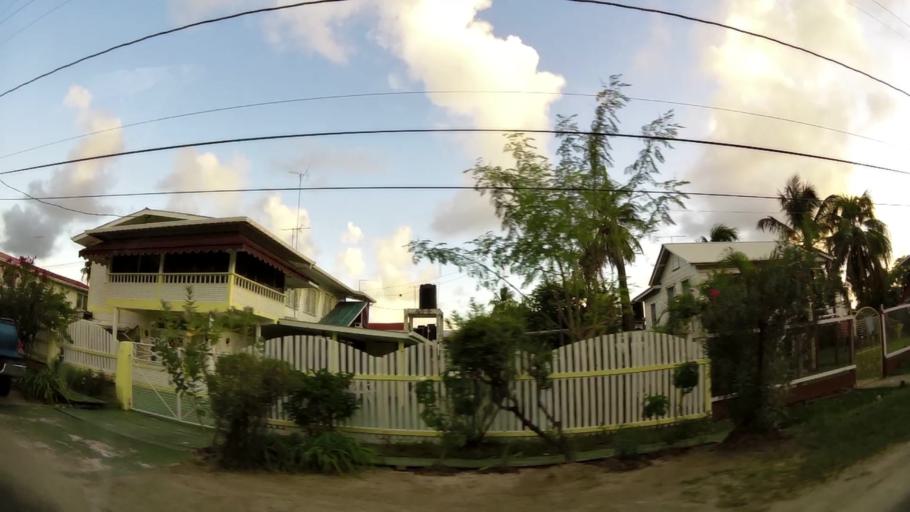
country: GY
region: Demerara-Mahaica
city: Georgetown
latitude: 6.8155
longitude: -58.1063
